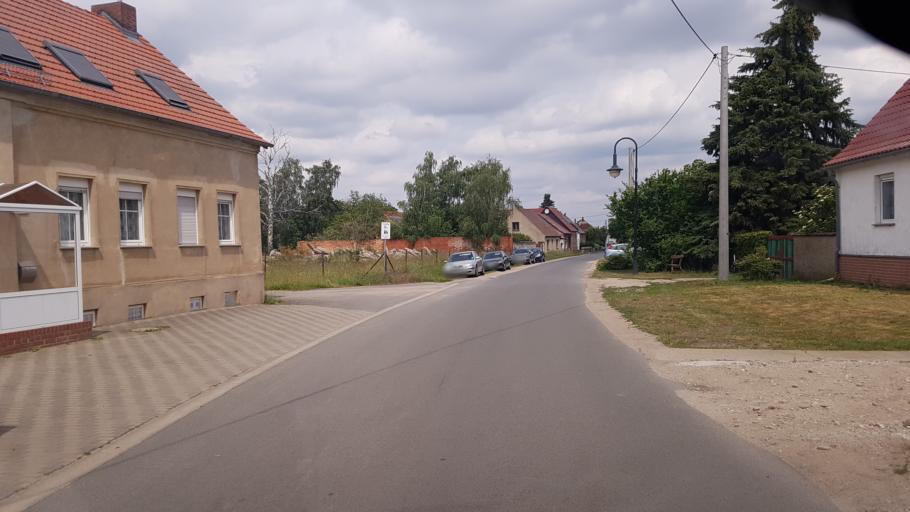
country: DE
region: Brandenburg
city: Dahme
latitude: 51.8521
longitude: 13.4372
